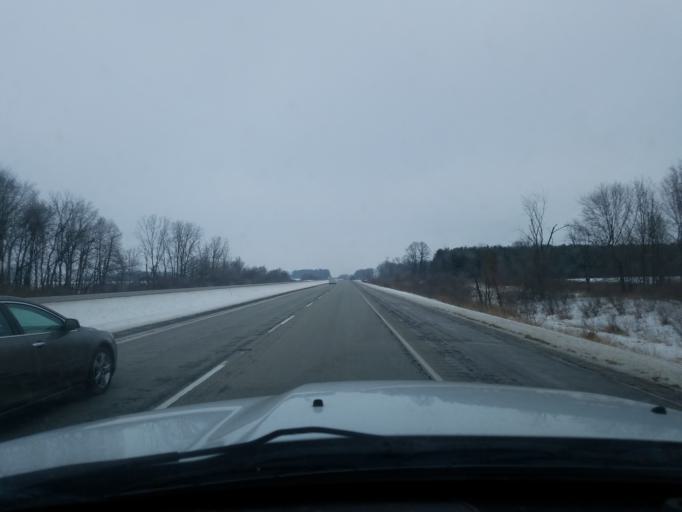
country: US
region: Indiana
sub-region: Fulton County
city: Rochester
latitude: 41.1512
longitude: -86.2396
